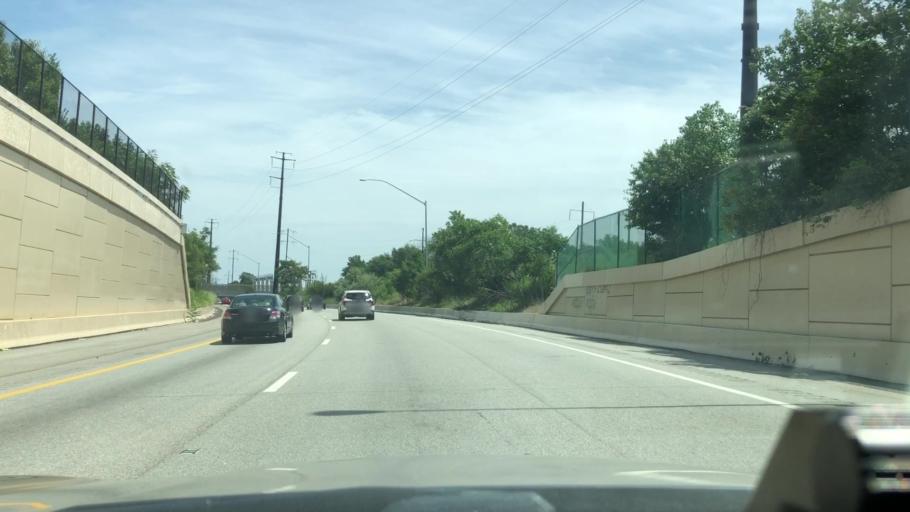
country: US
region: Pennsylvania
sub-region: Montgomery County
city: King of Prussia
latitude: 40.0803
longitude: -75.3948
